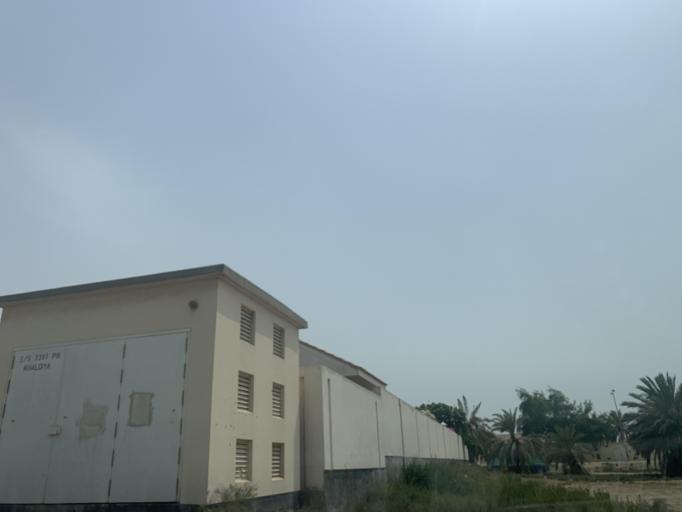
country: BH
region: Northern
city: Madinat `Isa
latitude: 26.1933
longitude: 50.4650
